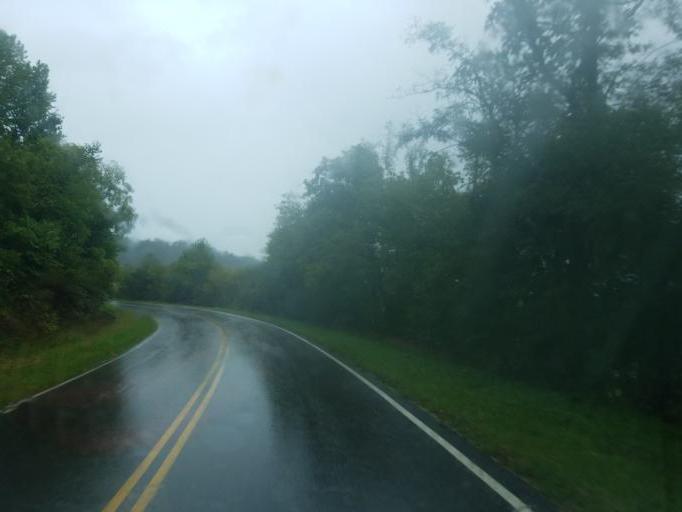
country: US
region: Kentucky
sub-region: Carter County
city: Grayson
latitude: 38.4911
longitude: -82.9879
